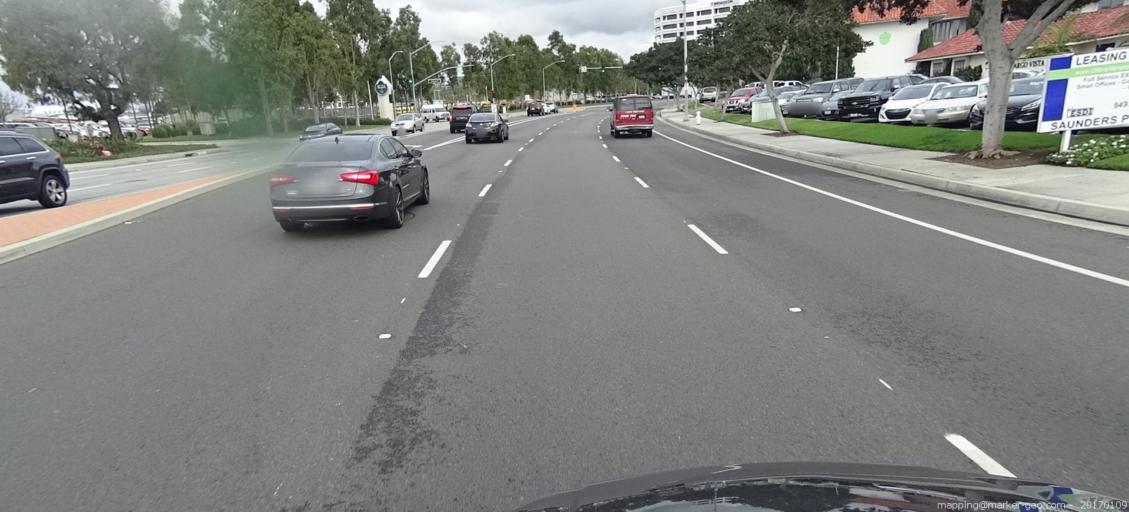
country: US
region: California
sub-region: Orange County
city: Irvine
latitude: 33.6706
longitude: -117.8668
